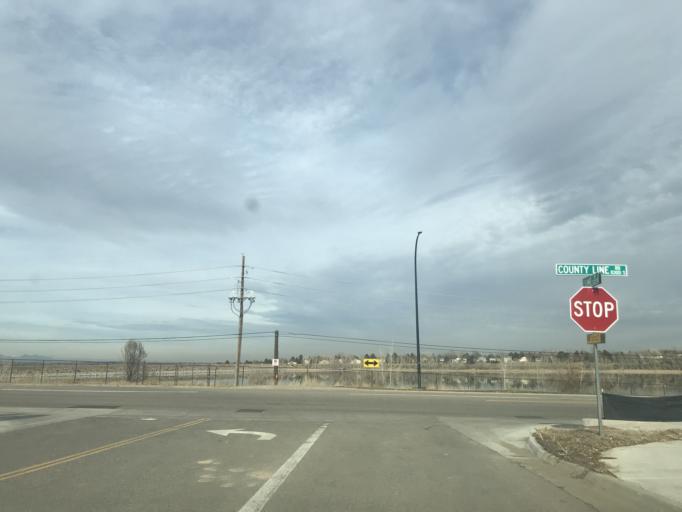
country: US
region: Colorado
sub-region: Arapahoe County
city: Columbine Valley
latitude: 39.5658
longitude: -105.0213
